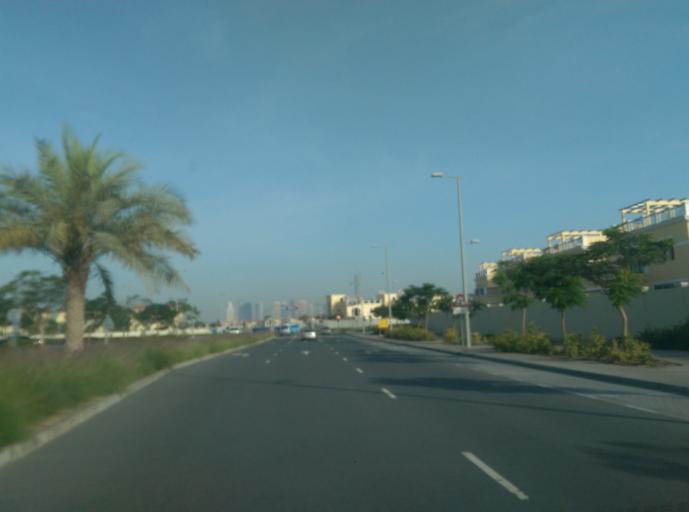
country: AE
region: Dubai
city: Dubai
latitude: 25.0428
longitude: 55.1688
